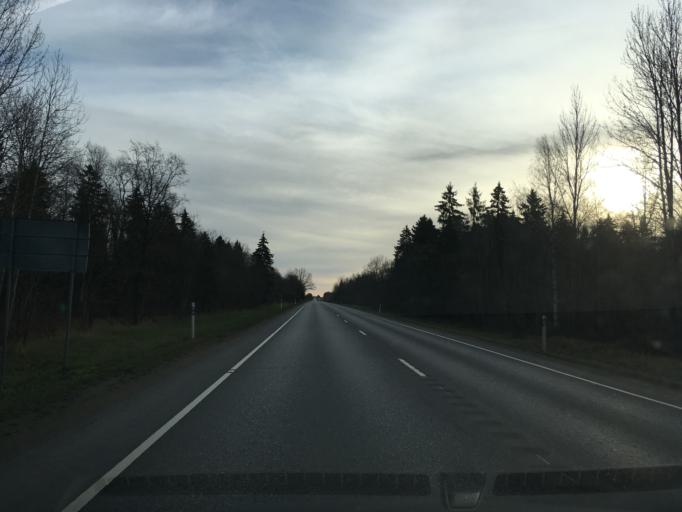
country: EE
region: Ida-Virumaa
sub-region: Kohtla-Jaerve linn
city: Kohtla-Jarve
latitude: 59.4175
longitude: 27.2893
